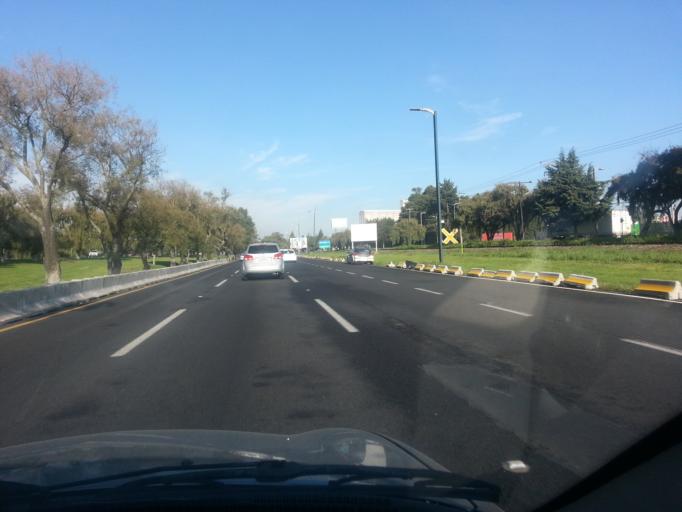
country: MX
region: Mexico
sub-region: San Mateo Atenco
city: Santa Maria la Asuncion
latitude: 19.2861
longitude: -99.5443
